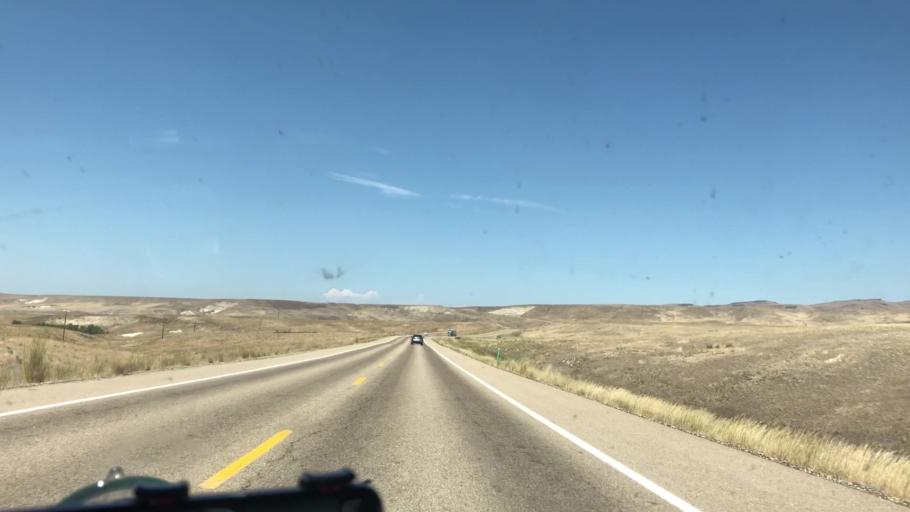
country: US
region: Idaho
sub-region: Owyhee County
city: Marsing
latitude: 43.2686
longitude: -117.0035
